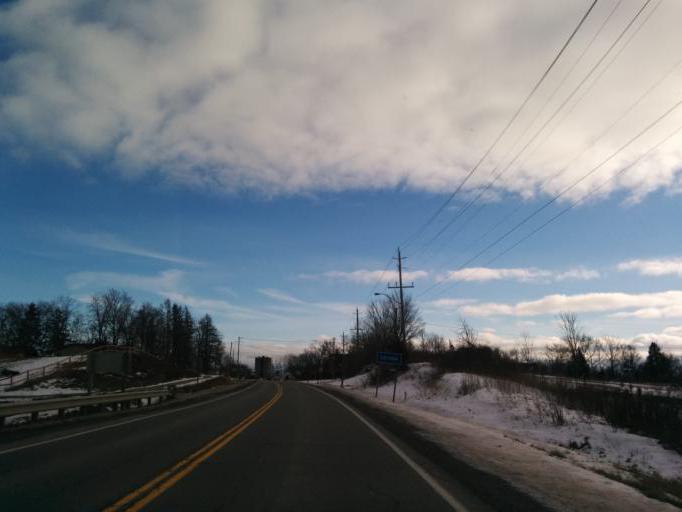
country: CA
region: Ontario
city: Ancaster
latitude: 42.9606
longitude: -79.8617
